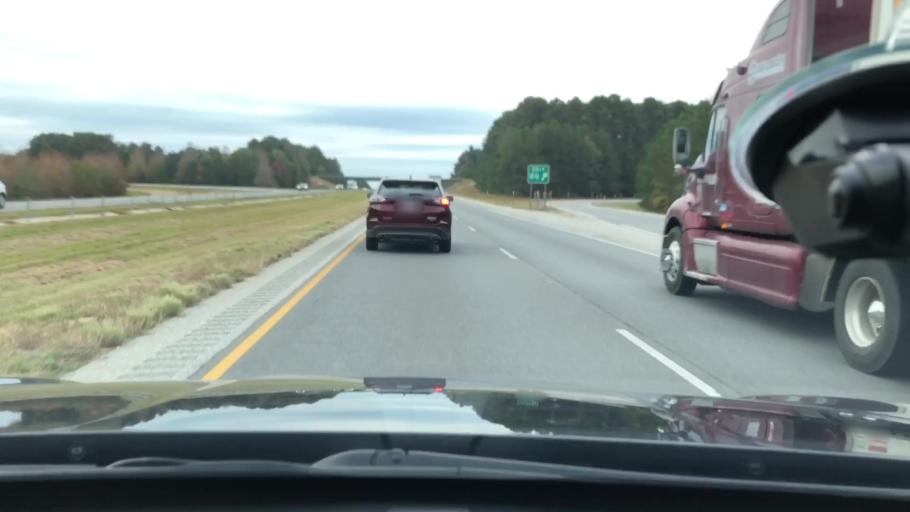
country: US
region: Arkansas
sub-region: Clark County
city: Arkadelphia
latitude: 34.0702
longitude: -93.1222
